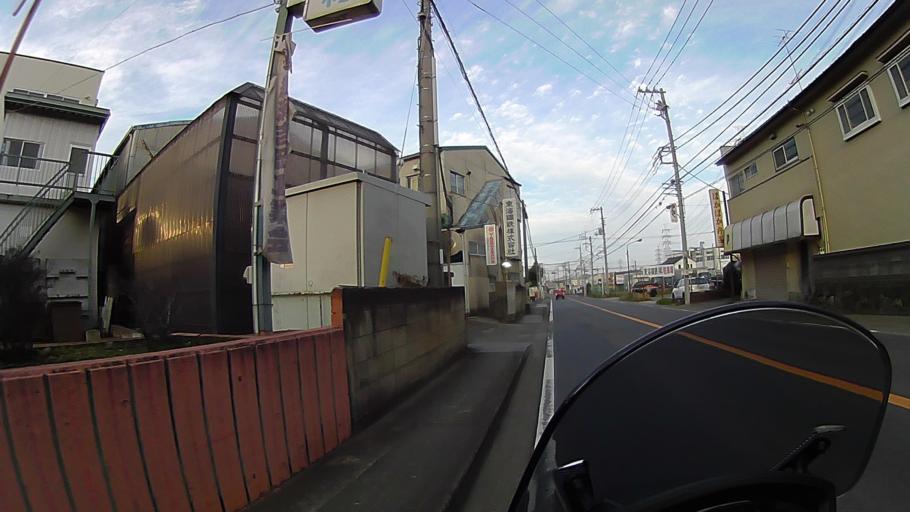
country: JP
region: Kanagawa
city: Atsugi
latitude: 35.4211
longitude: 139.4243
